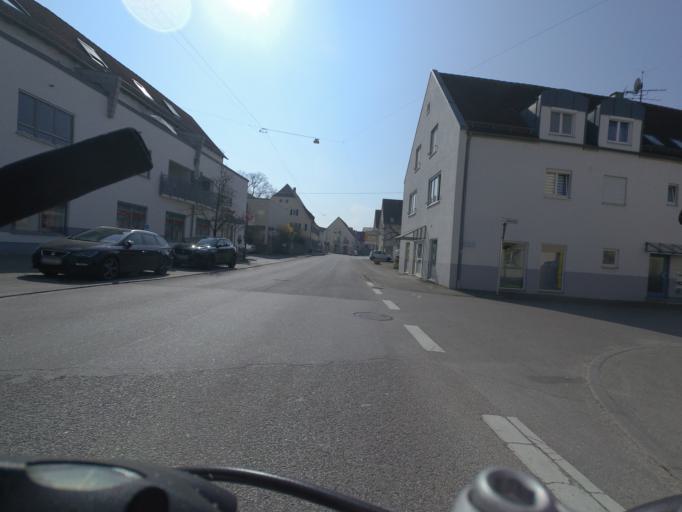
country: DE
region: Baden-Wuerttemberg
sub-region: Regierungsbezirk Stuttgart
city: Oberboihingen
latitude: 48.6486
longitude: 9.3662
